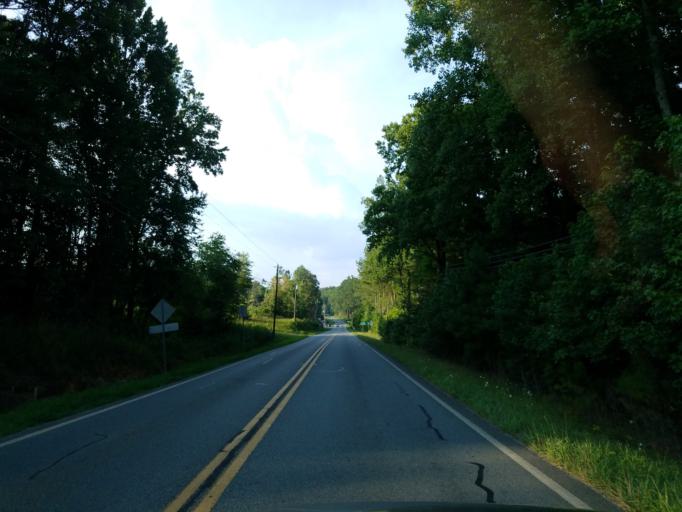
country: US
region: Georgia
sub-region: Gilmer County
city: Ellijay
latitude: 34.6384
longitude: -84.5093
